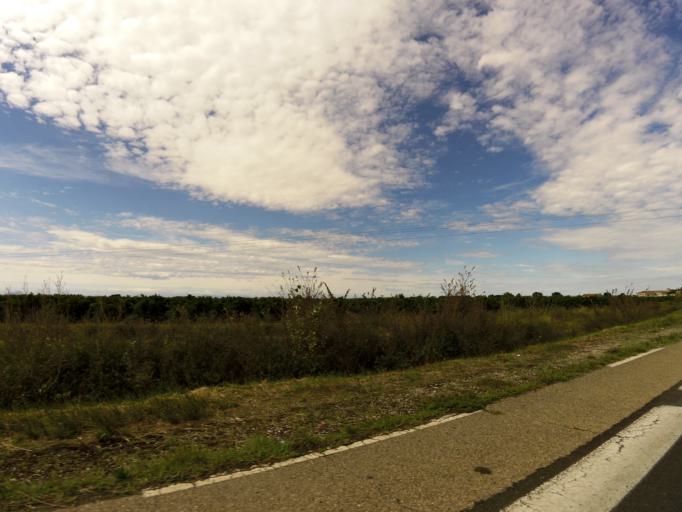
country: FR
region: Languedoc-Roussillon
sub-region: Departement du Gard
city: Aimargues
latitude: 43.6645
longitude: 4.2103
